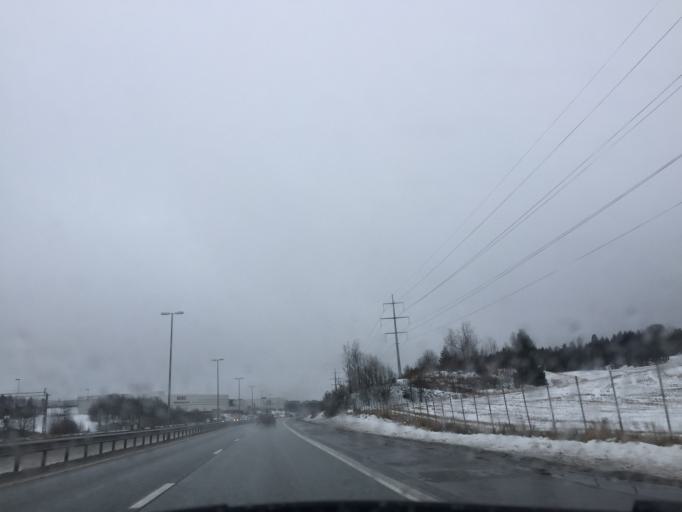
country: NO
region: Akershus
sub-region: Vestby
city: Vestby
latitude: 59.5971
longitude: 10.7388
